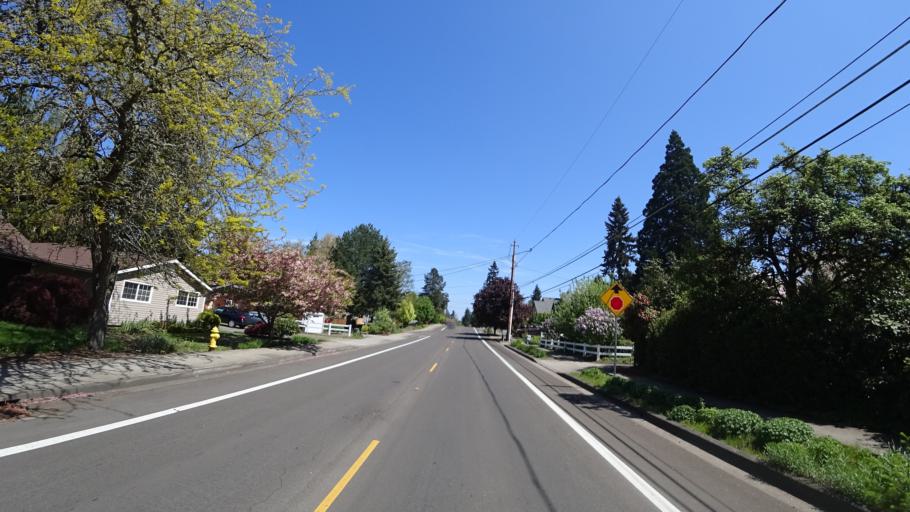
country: US
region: Oregon
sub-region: Washington County
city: Hillsboro
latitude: 45.5148
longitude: -122.9630
